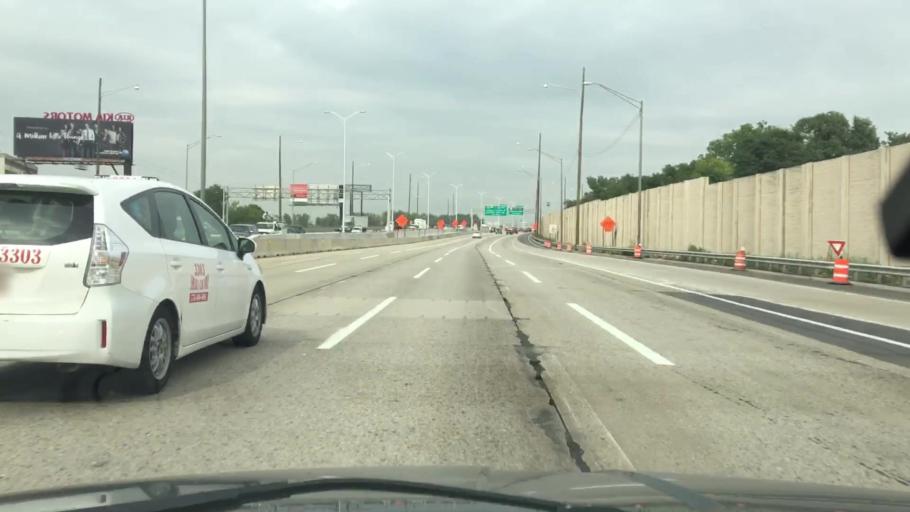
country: US
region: Illinois
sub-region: Cook County
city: Schiller Park
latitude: 41.9527
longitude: -87.8818
